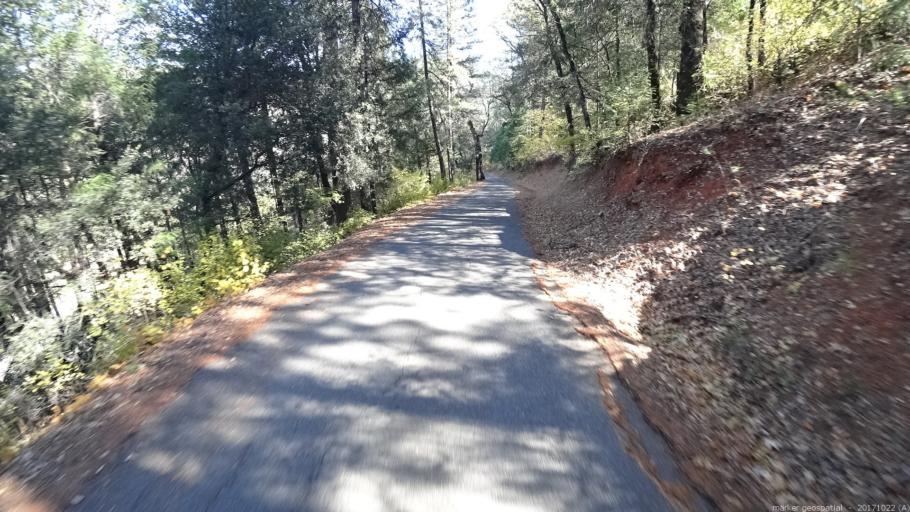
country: US
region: California
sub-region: Shasta County
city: Central Valley (historical)
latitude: 40.9424
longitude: -122.4294
